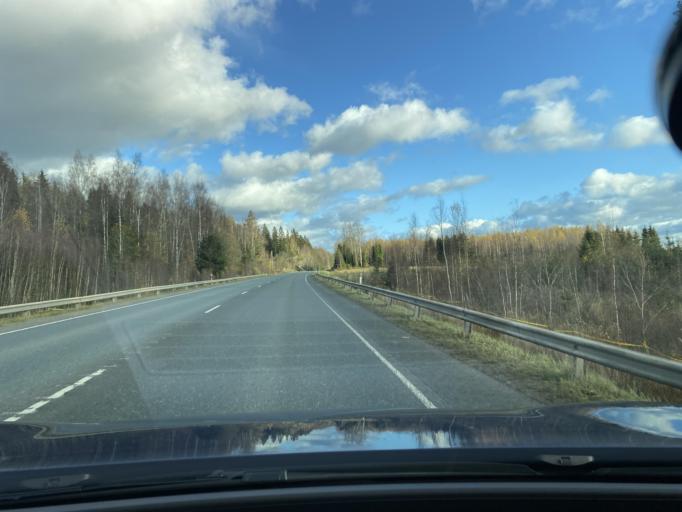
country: FI
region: Haeme
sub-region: Riihimaeki
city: Hausjaervi
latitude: 60.7809
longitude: 24.8607
